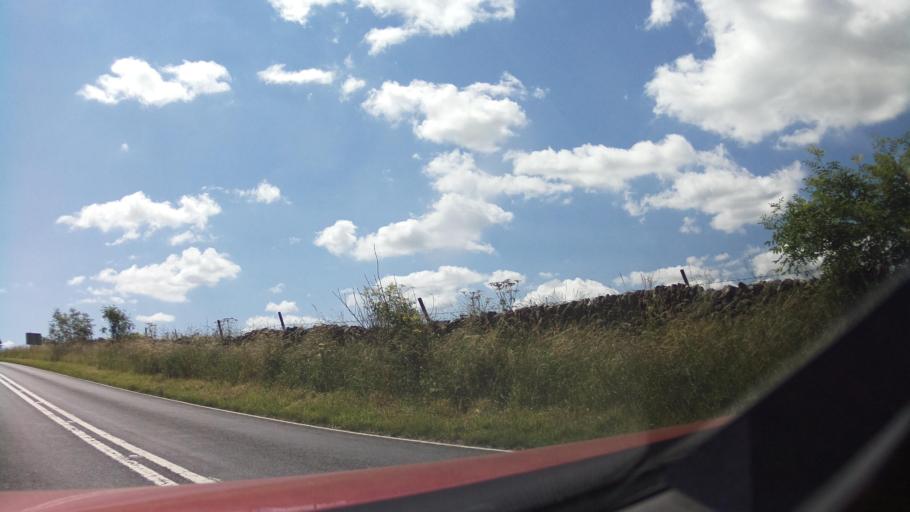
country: GB
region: England
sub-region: Derbyshire
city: Ashbourne
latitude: 53.1289
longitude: -1.7546
